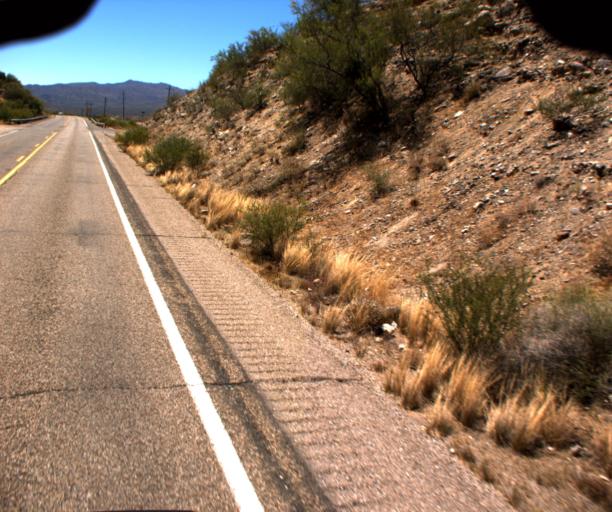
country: US
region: Arizona
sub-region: Pinal County
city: Kearny
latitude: 33.0805
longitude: -110.9249
